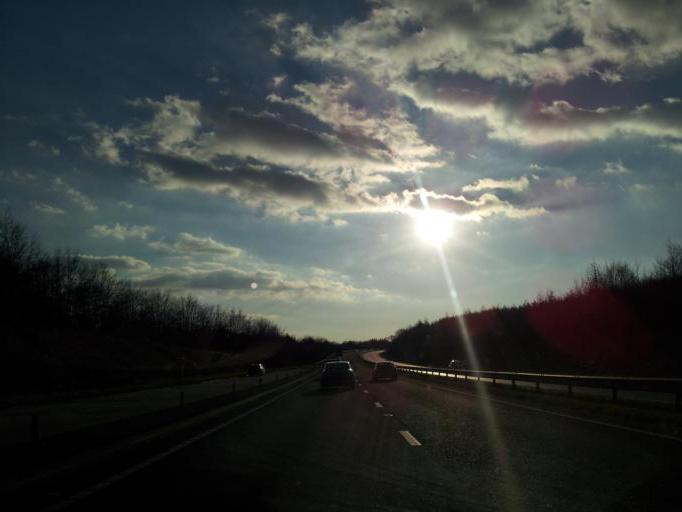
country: GB
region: England
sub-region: Devon
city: Tavistock
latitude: 50.6792
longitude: -4.2105
